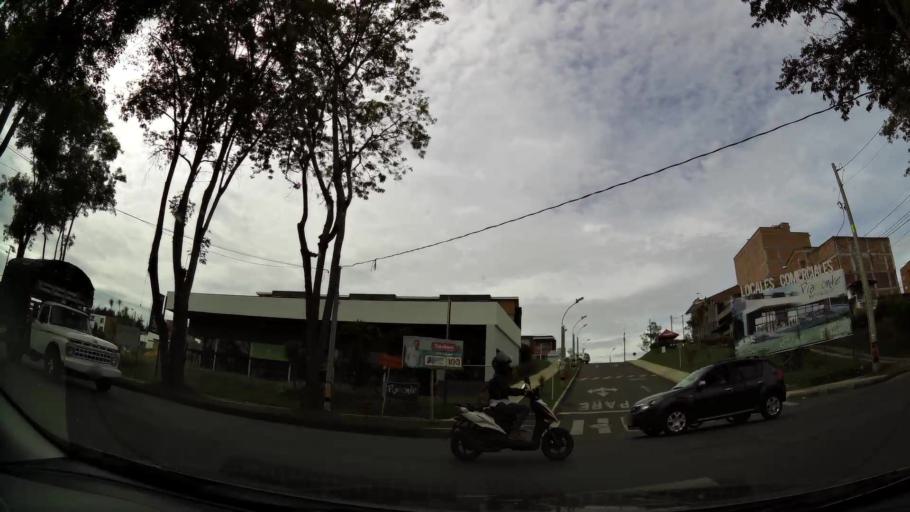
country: CO
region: Antioquia
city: Rionegro
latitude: 6.1515
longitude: -75.3822
